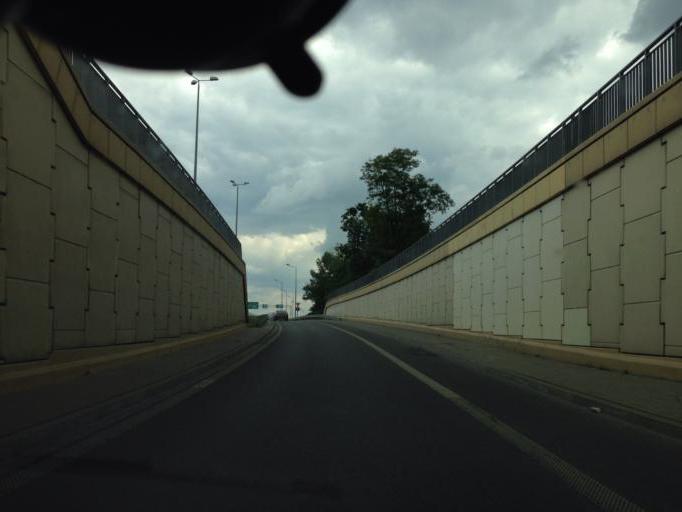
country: PL
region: Masovian Voivodeship
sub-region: Warszawa
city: Bielany
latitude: 52.2568
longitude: 20.9487
